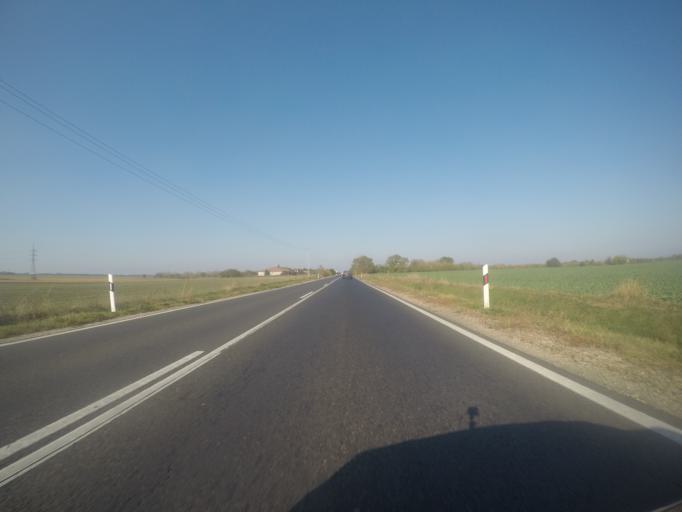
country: HU
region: Fejer
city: Baracs
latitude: 46.8477
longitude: 18.9112
